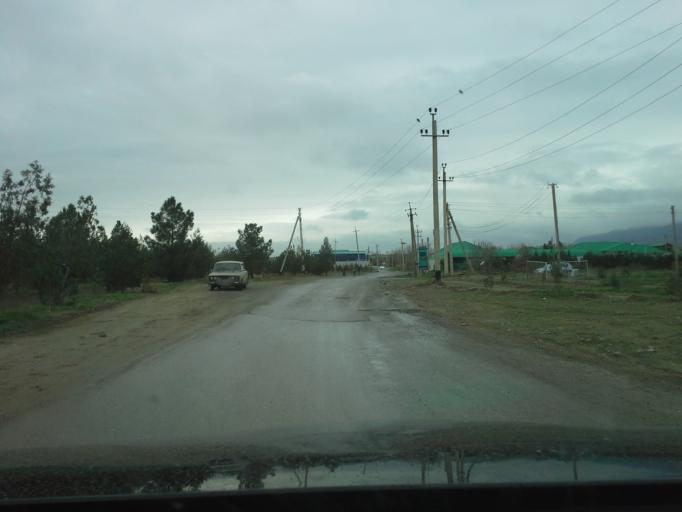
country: TM
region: Ahal
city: Abadan
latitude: 37.9667
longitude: 58.2288
